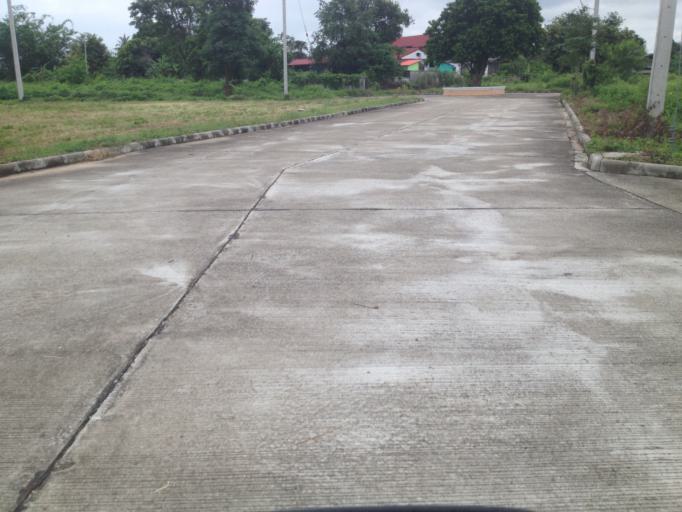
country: TH
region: Chiang Mai
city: Hang Dong
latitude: 18.7087
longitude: 98.9106
